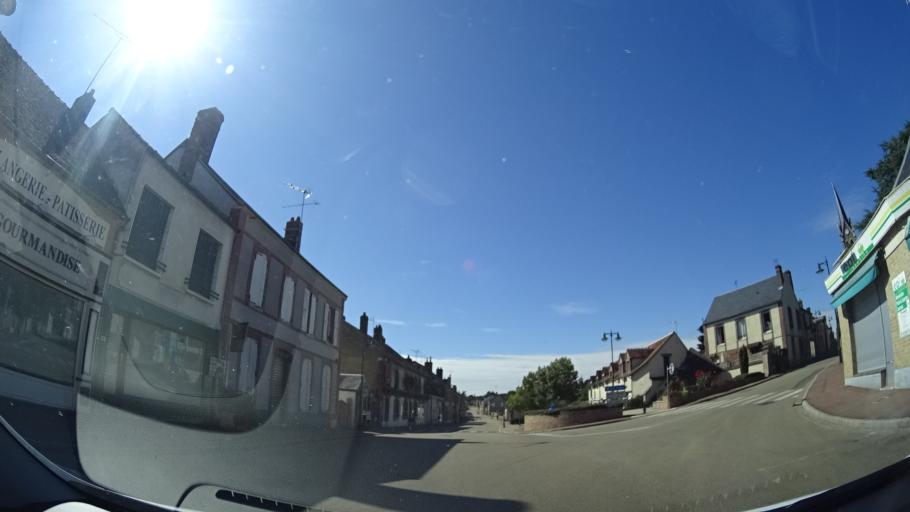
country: FR
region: Centre
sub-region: Departement du Loiret
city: Douchy
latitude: 47.9427
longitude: 3.0543
